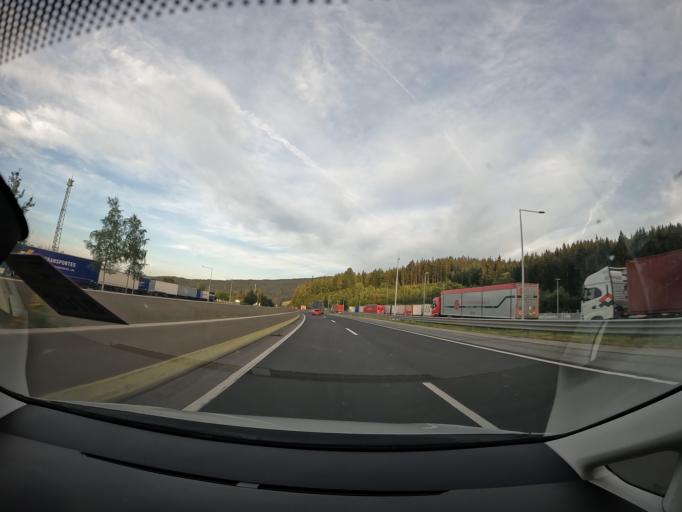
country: AT
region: Styria
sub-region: Politischer Bezirk Voitsberg
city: Voitsberg
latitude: 46.9891
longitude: 15.1121
